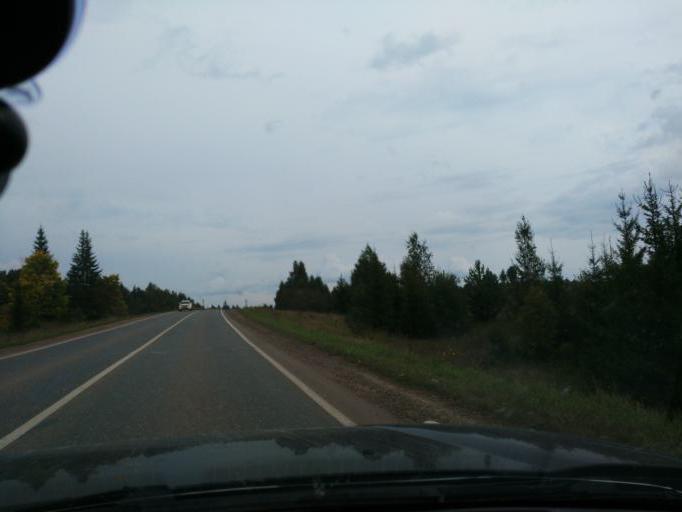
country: RU
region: Perm
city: Chernushka
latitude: 56.5082
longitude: 55.8798
